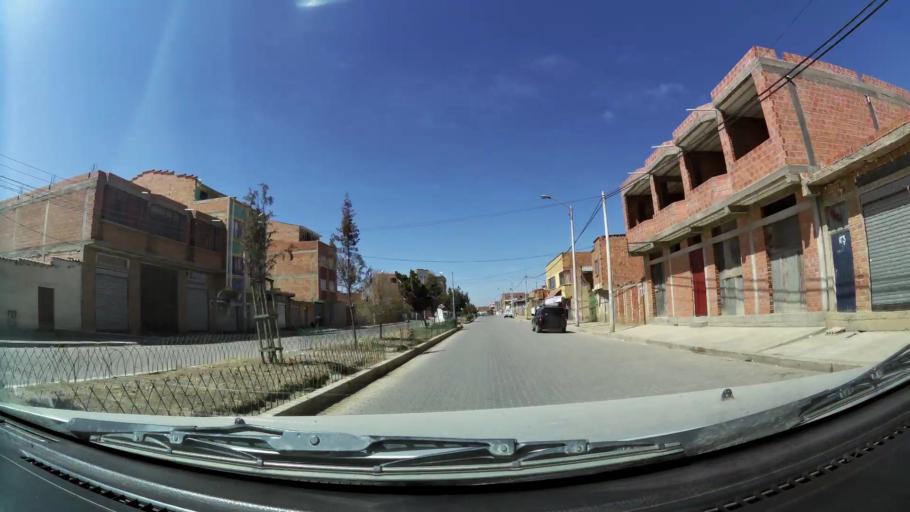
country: BO
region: La Paz
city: La Paz
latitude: -16.5349
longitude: -68.1616
